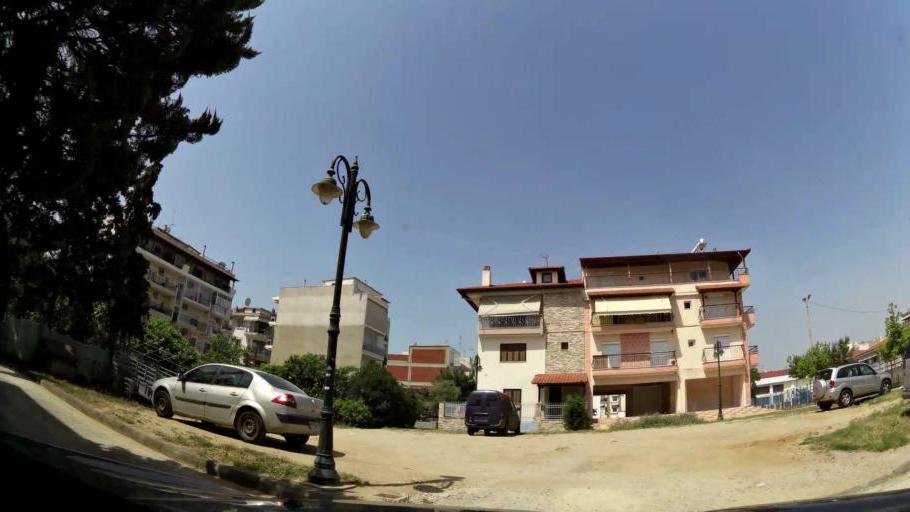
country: GR
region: Central Macedonia
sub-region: Nomos Thessalonikis
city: Evosmos
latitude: 40.6689
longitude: 22.9170
